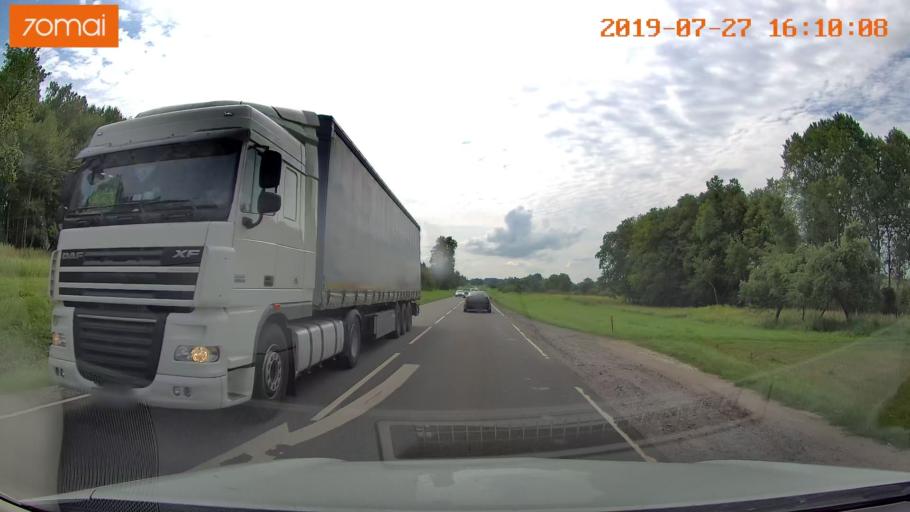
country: RU
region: Kaliningrad
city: Chernyakhovsk
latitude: 54.6370
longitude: 21.7017
